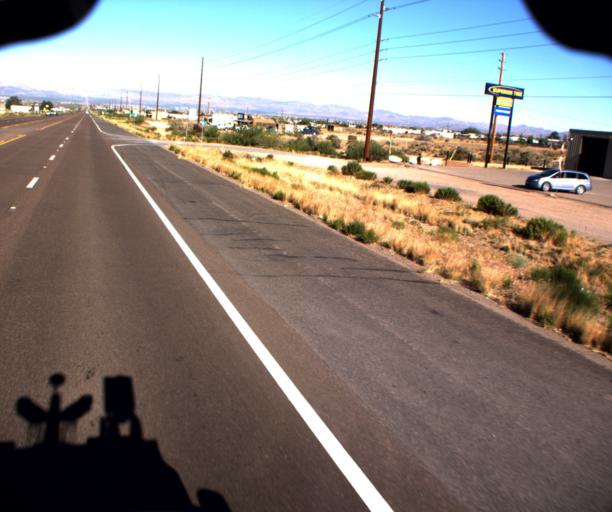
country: US
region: Arizona
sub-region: Mohave County
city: Golden Valley
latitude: 35.2198
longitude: -114.1691
